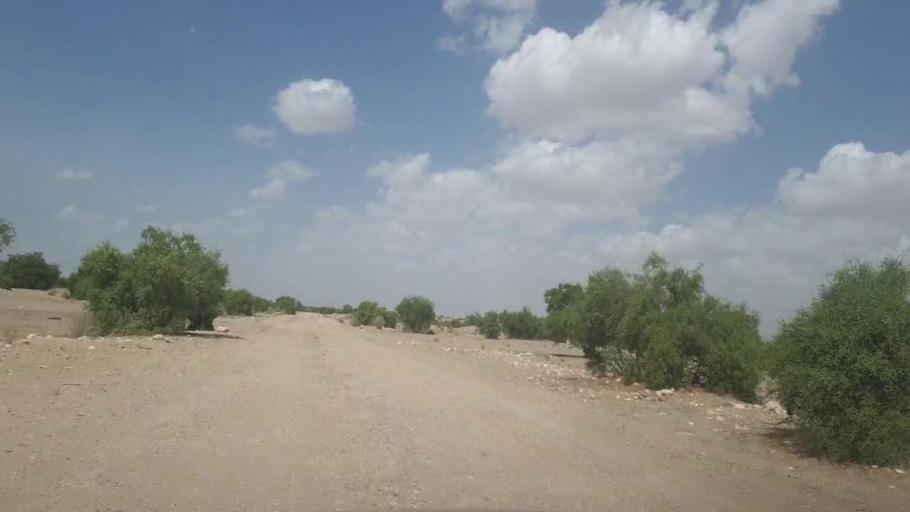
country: PK
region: Sindh
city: Kot Diji
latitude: 27.2618
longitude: 69.1737
